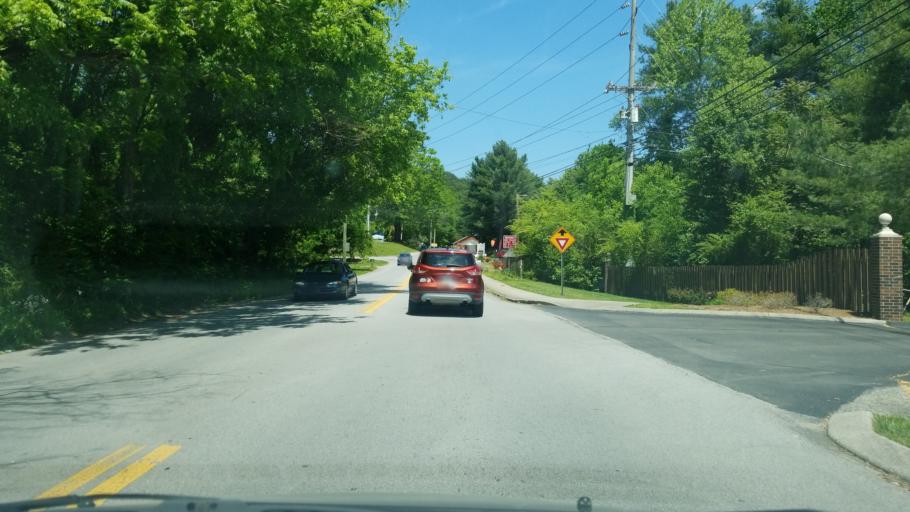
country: US
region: Tennessee
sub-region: Hamilton County
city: Signal Mountain
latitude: 35.1057
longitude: -85.3267
